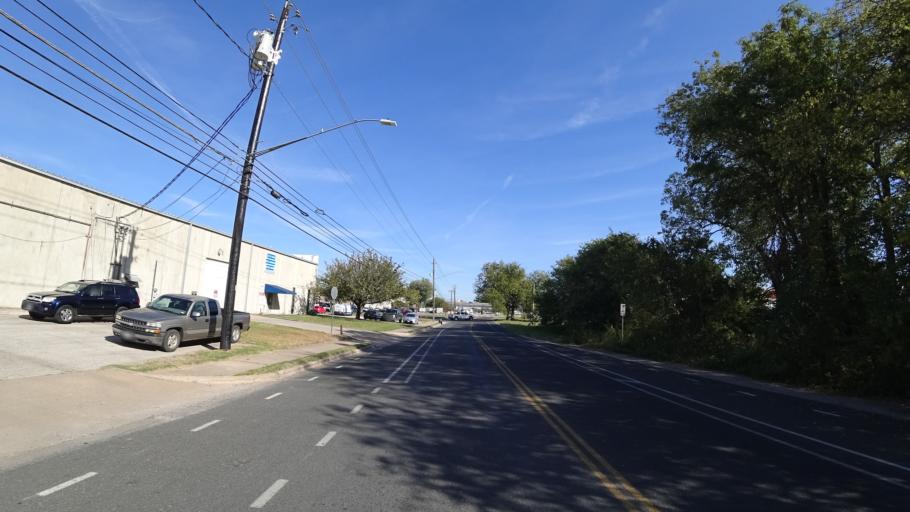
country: US
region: Texas
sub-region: Travis County
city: Austin
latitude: 30.2546
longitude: -97.6822
